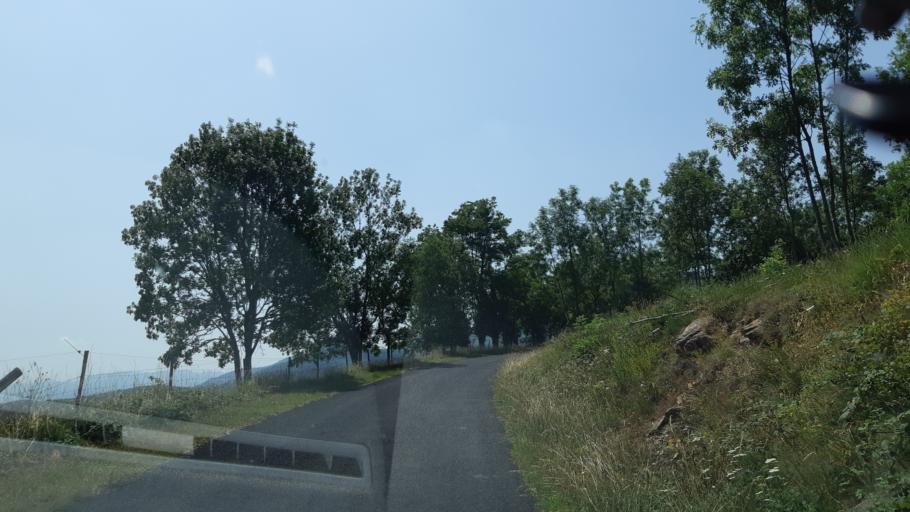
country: FR
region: Languedoc-Roussillon
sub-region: Departement des Pyrenees-Orientales
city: Arles
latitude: 42.5440
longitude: 2.5815
